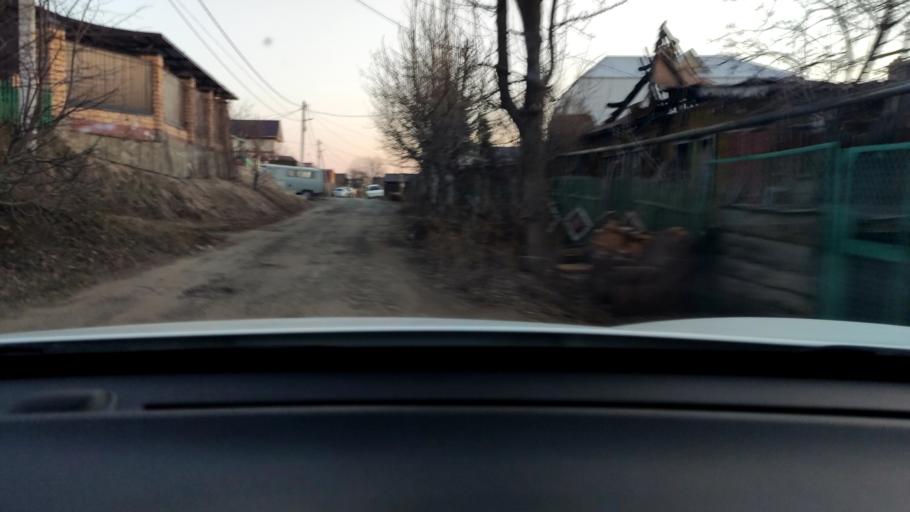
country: RU
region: Tatarstan
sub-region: Gorod Kazan'
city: Kazan
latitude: 55.7323
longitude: 49.1543
